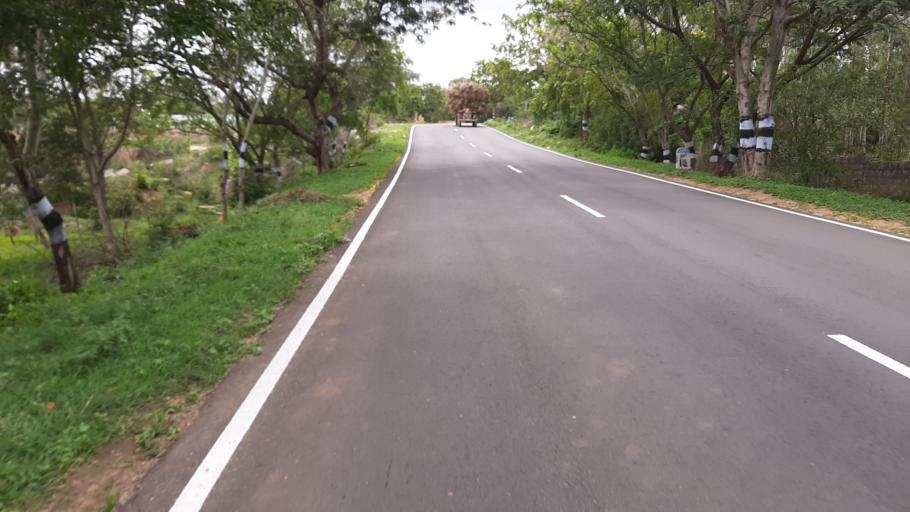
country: IN
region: Tamil Nadu
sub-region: Krishnagiri
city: Denkanikota
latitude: 12.5405
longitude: 77.7626
